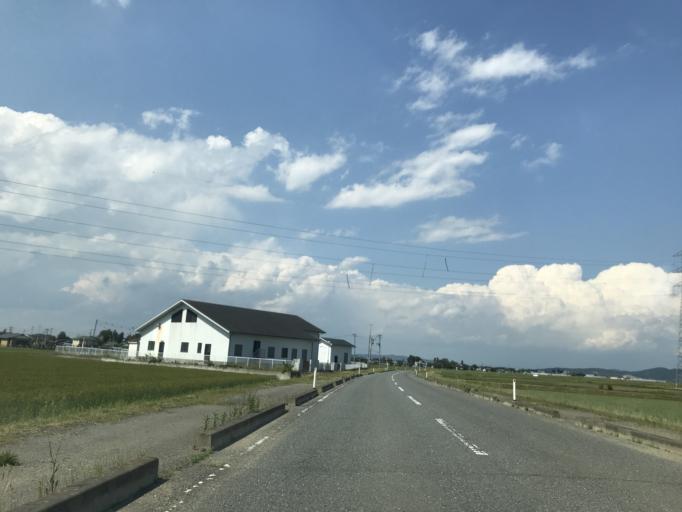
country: JP
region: Miyagi
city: Matsushima
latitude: 38.4515
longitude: 141.1123
